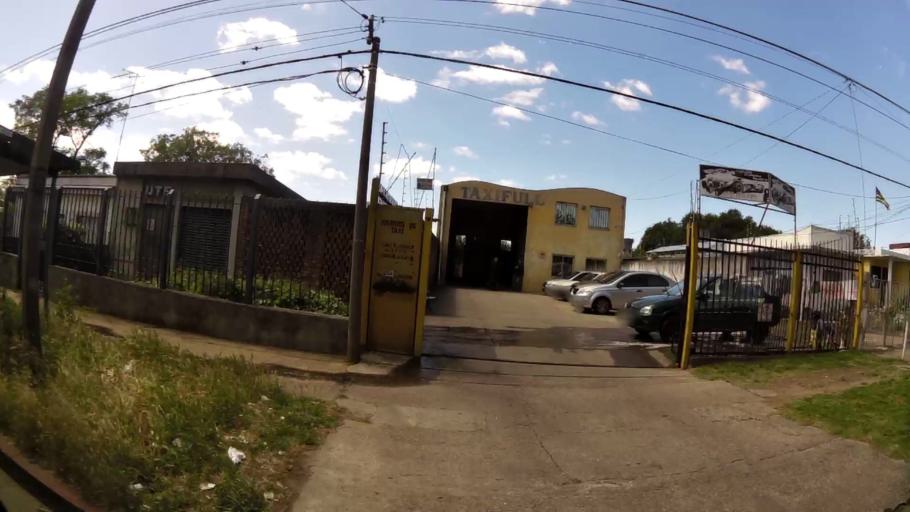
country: UY
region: Montevideo
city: Montevideo
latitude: -34.8516
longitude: -56.1367
